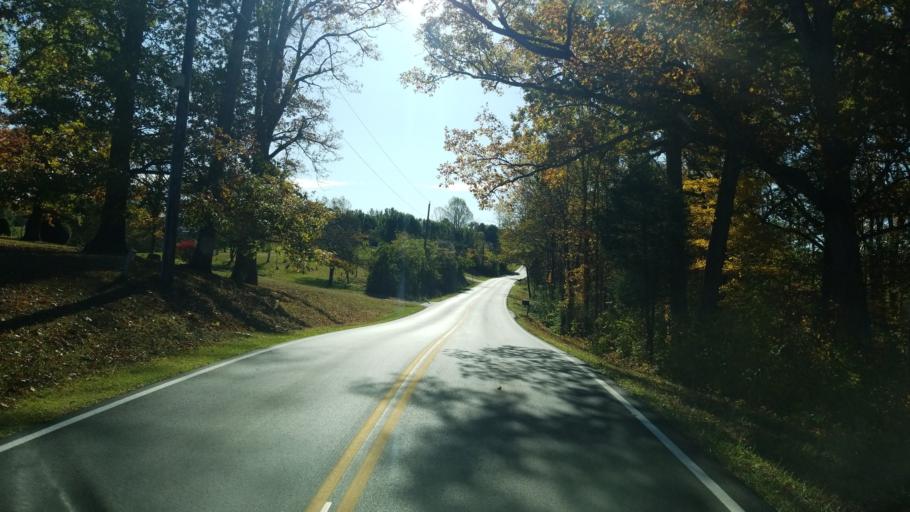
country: US
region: Ohio
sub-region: Warren County
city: Morrow
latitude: 39.3989
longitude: -84.0734
